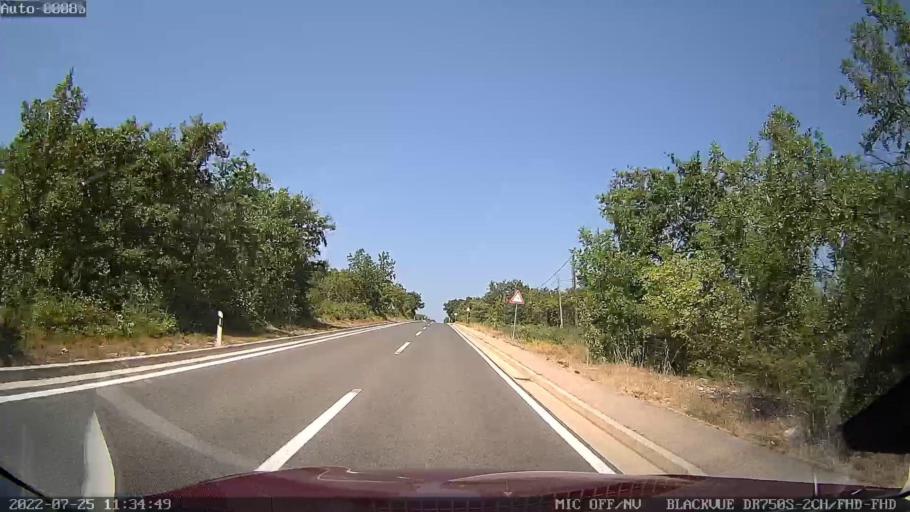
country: HR
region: Zadarska
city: Posedarje
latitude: 44.2312
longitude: 15.4170
